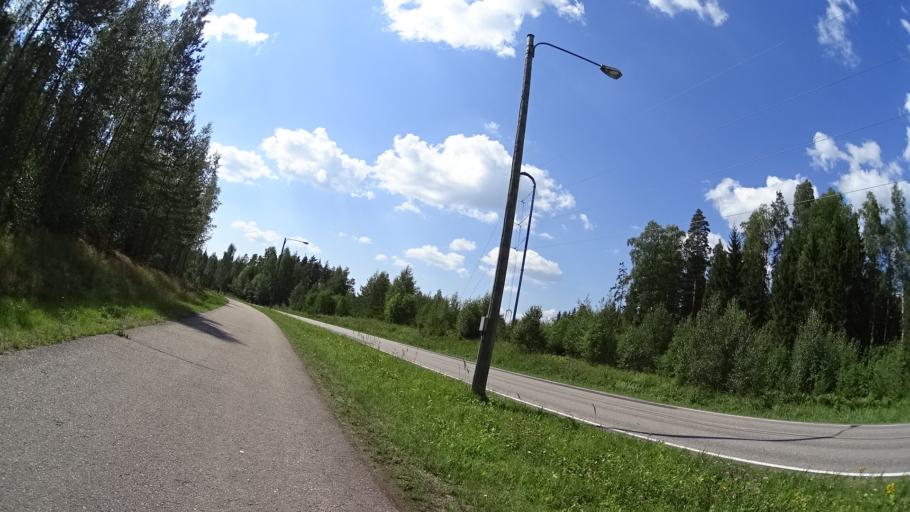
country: FI
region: Uusimaa
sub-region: Helsinki
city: Tuusula
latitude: 60.3536
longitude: 24.9969
